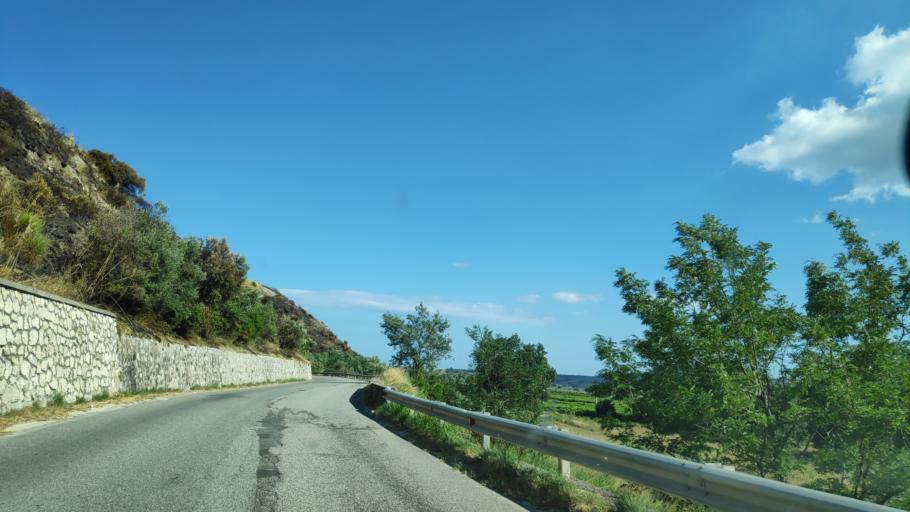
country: IT
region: Calabria
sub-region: Provincia di Reggio Calabria
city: Monasterace
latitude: 38.4597
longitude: 16.5217
